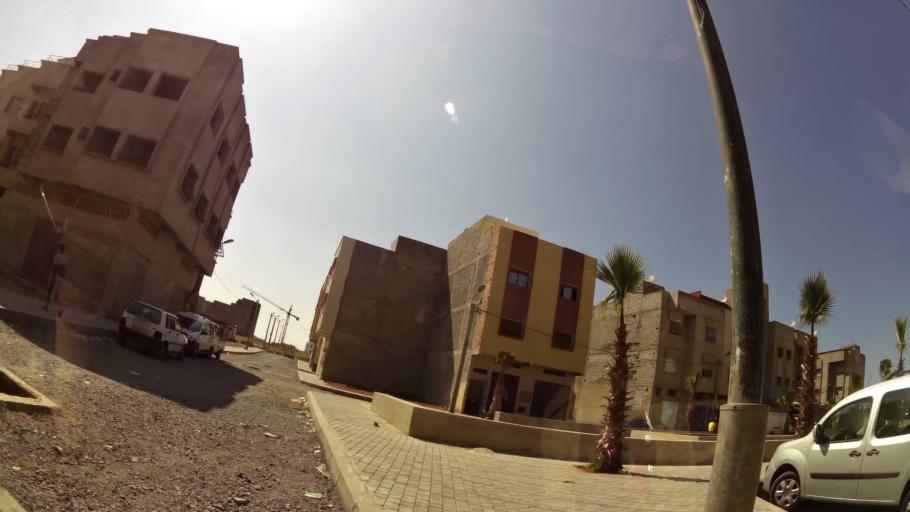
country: MA
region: Rabat-Sale-Zemmour-Zaer
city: Sale
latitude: 34.0707
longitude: -6.7670
